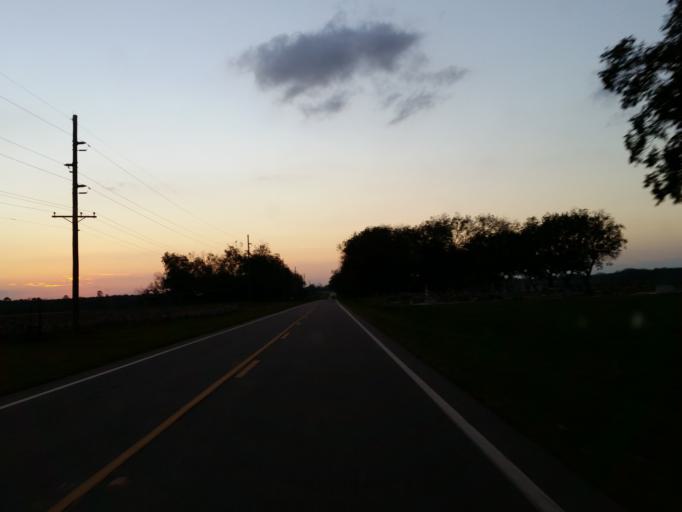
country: US
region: Georgia
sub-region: Dooly County
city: Vienna
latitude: 32.1234
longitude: -83.7432
